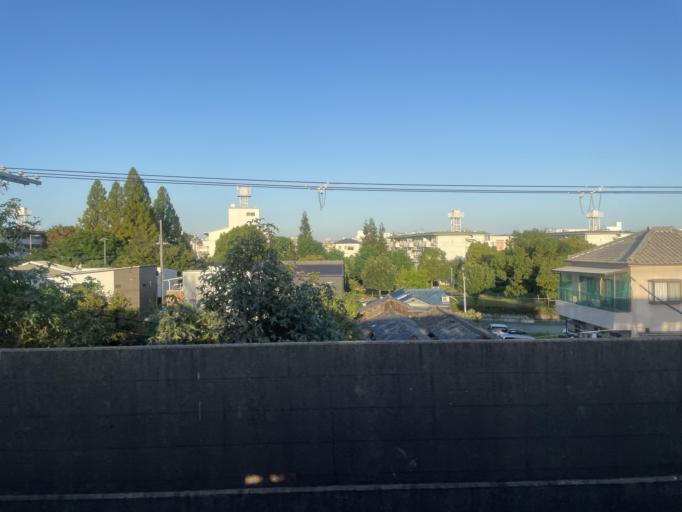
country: JP
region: Osaka
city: Matsubara
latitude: 34.6013
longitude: 135.5323
